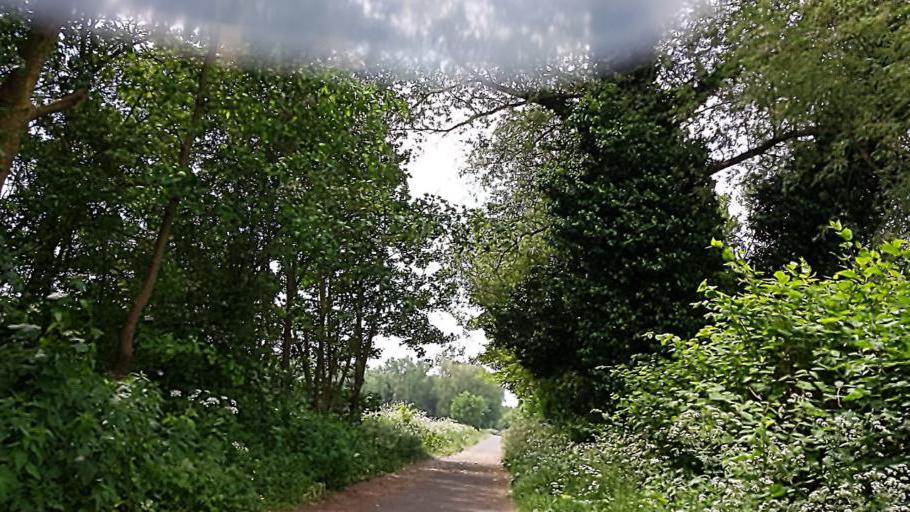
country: BE
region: Wallonia
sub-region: Province du Hainaut
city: Peruwelz
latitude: 50.5085
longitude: 3.5763
